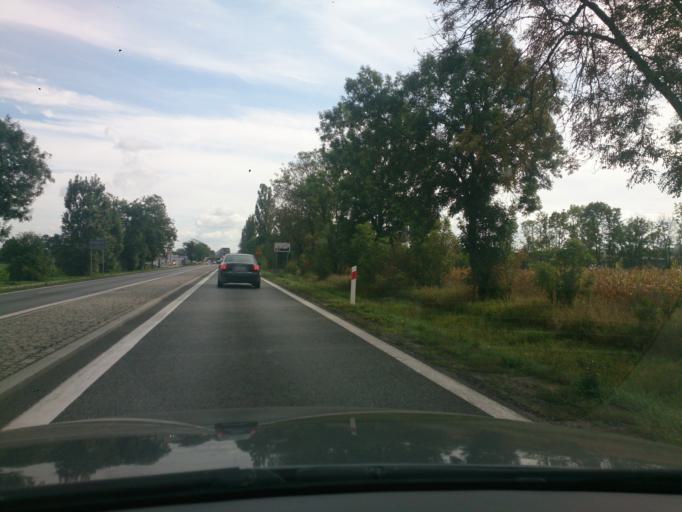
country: PL
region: Kujawsko-Pomorskie
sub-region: Grudziadz
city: Grudziadz
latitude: 53.4908
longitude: 18.7146
